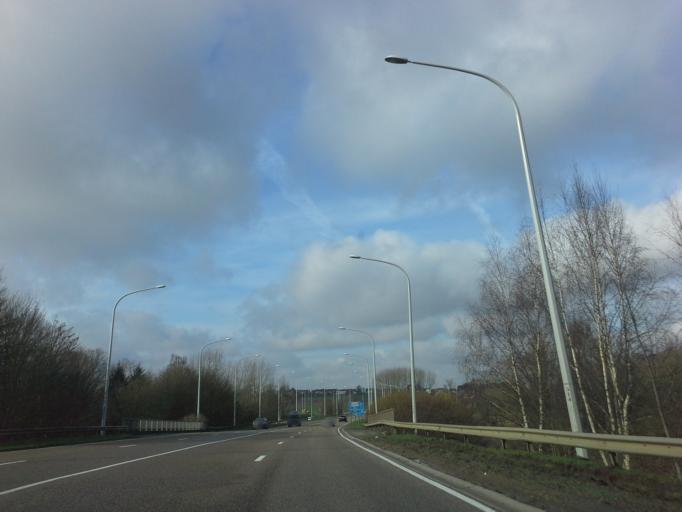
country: BE
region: Flanders
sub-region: Provincie Vlaams-Brabant
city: Tienen
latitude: 50.7925
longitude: 4.9350
